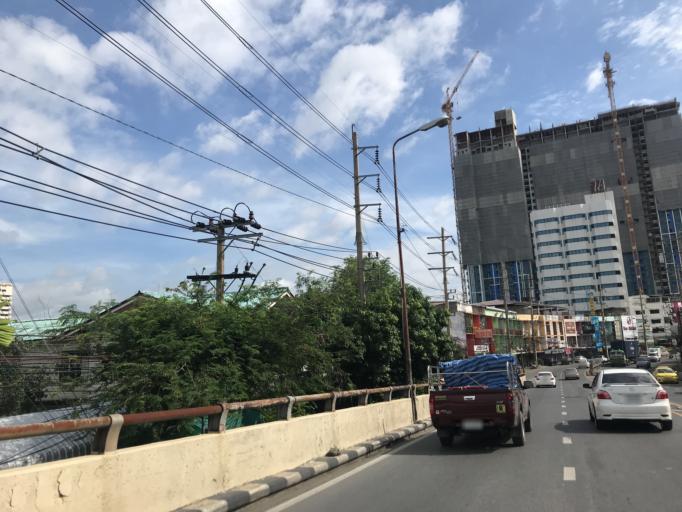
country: TH
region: Bangkok
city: Watthana
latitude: 13.7383
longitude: 100.5985
